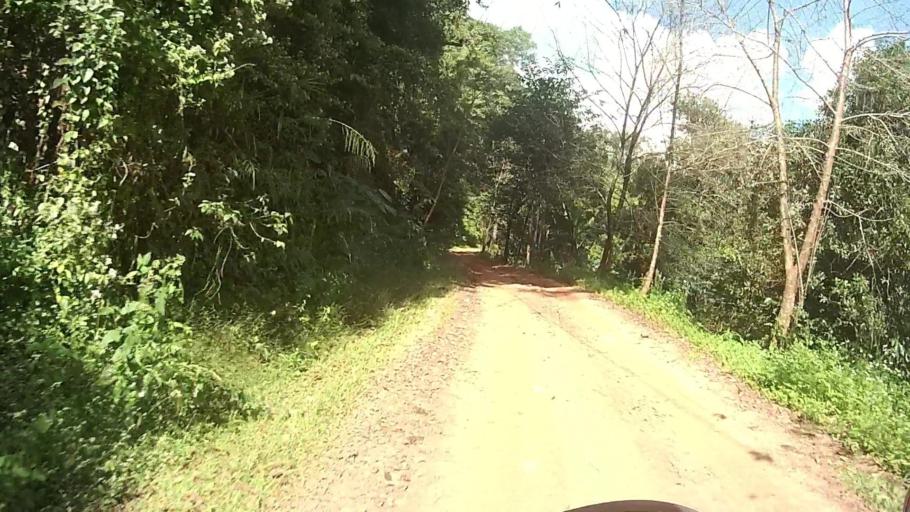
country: TH
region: Lampang
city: Mueang Pan
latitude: 18.9112
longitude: 99.4121
